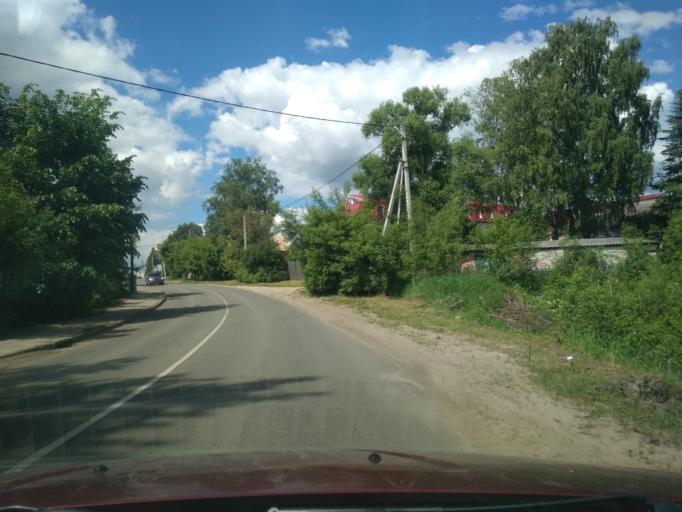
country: RU
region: Vladimir
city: Melenki
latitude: 55.3392
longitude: 41.6435
